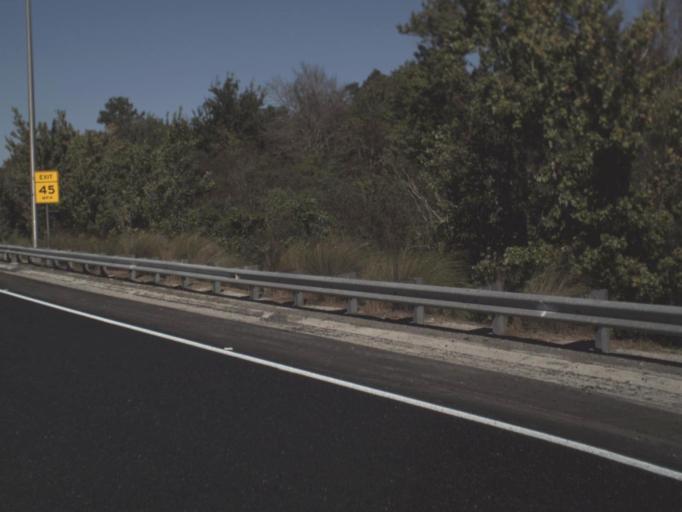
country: US
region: Florida
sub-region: Seminole County
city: Lake Mary
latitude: 28.7822
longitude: -81.3003
